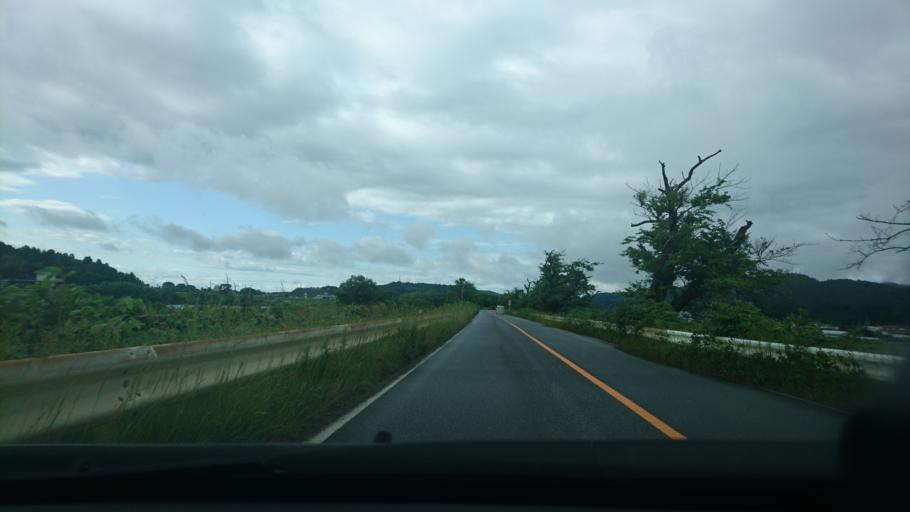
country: JP
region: Miyagi
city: Wakuya
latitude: 38.6443
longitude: 141.2867
